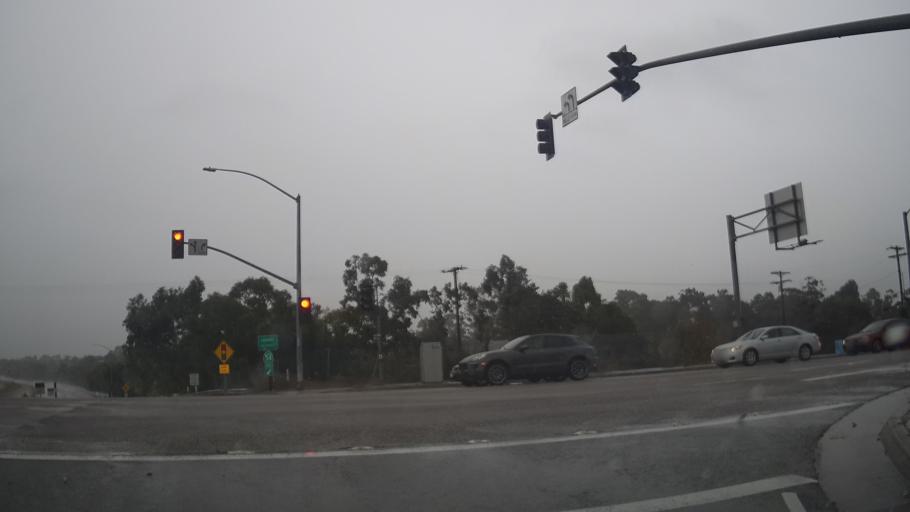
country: US
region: California
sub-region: San Diego County
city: Bonita
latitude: 32.6631
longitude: -117.0575
